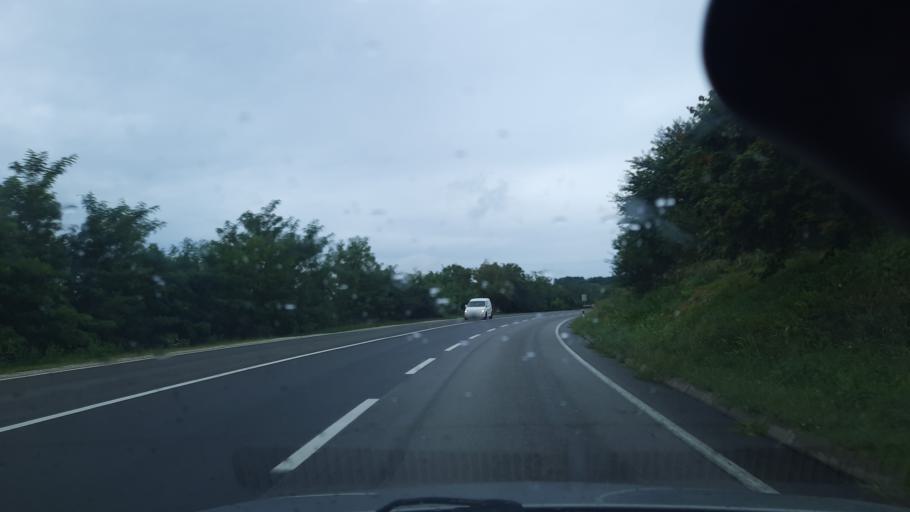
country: RS
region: Central Serbia
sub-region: Sumadijski Okrug
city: Knic
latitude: 43.9497
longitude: 20.8034
